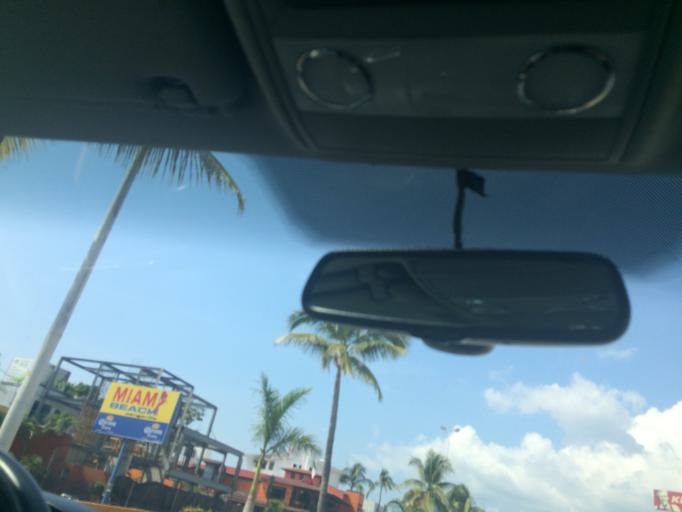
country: MX
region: Colima
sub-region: Manzanillo
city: Manzanillo
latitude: 19.1038
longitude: -104.3314
